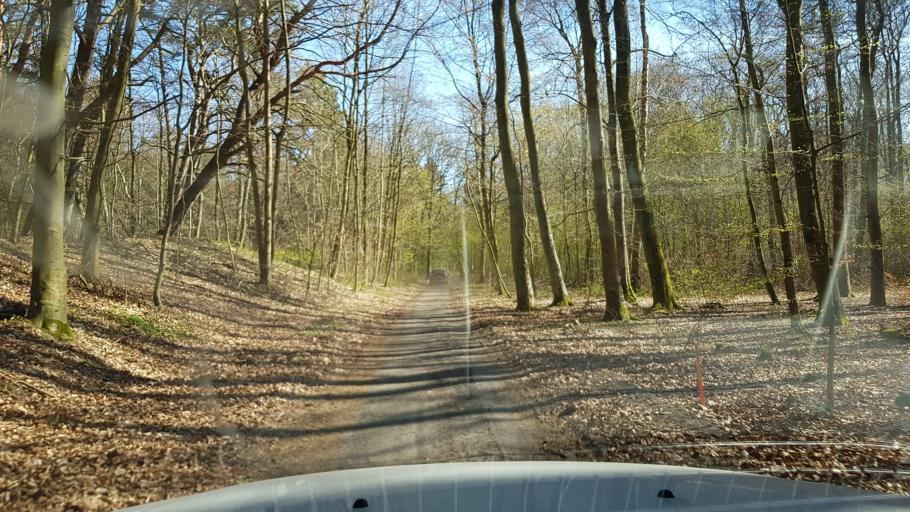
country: PL
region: West Pomeranian Voivodeship
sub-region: Powiat koszalinski
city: Mielno
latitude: 54.2538
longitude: 16.0082
